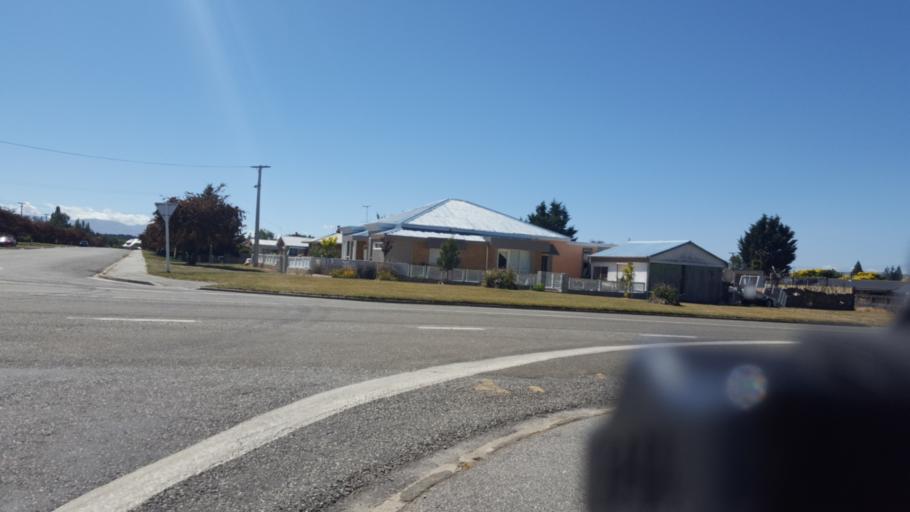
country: NZ
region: Otago
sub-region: Dunedin City
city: Dunedin
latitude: -45.1281
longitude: 170.1004
